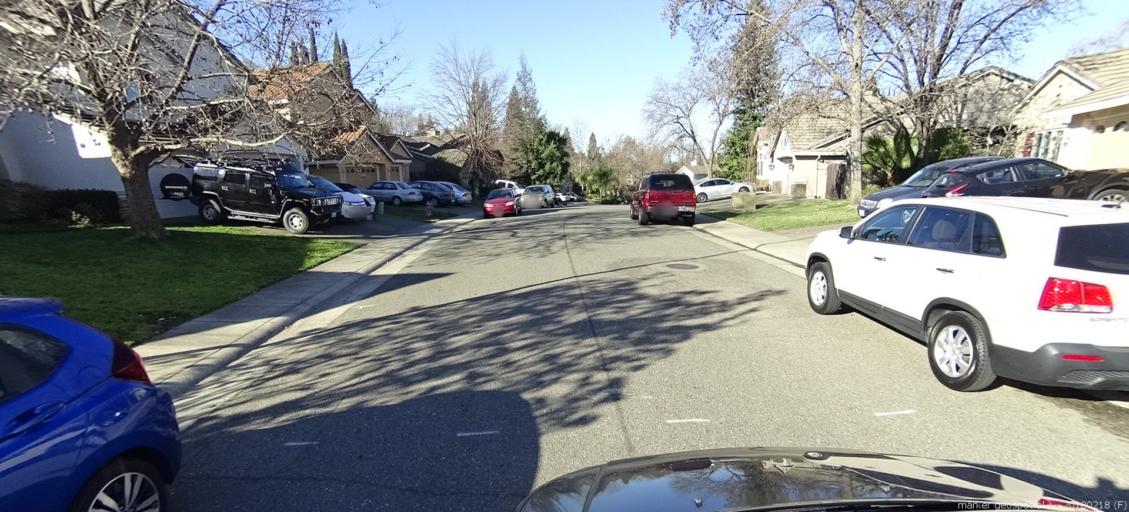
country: US
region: California
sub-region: Sacramento County
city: Orangevale
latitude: 38.6755
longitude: -121.2406
